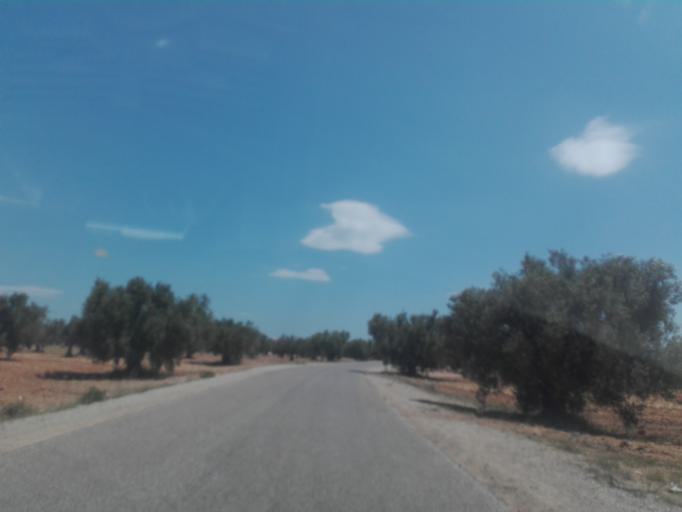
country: TN
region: Safaqis
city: Sfax
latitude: 34.6201
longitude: 10.6147
